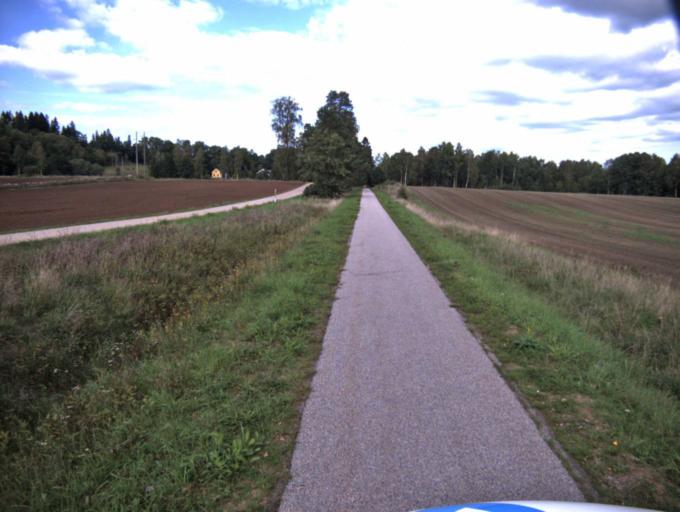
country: SE
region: Vaestra Goetaland
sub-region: Ulricehamns Kommun
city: Ulricehamn
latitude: 57.8420
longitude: 13.4214
